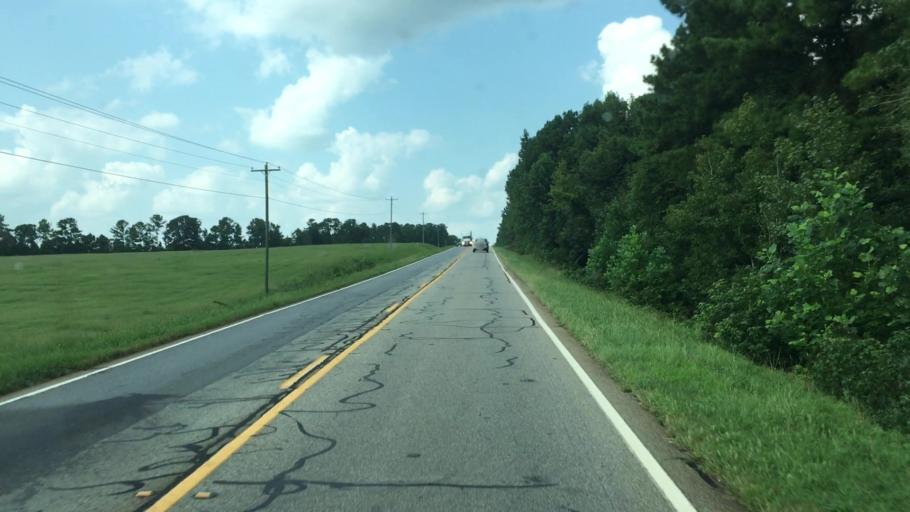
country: US
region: Georgia
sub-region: Jasper County
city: Monticello
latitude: 33.2518
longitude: -83.7201
